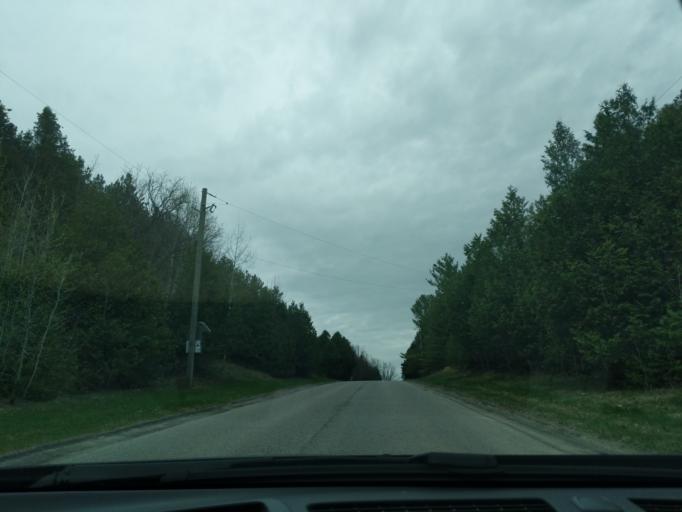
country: CA
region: Ontario
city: Orangeville
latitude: 44.0163
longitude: -79.9679
